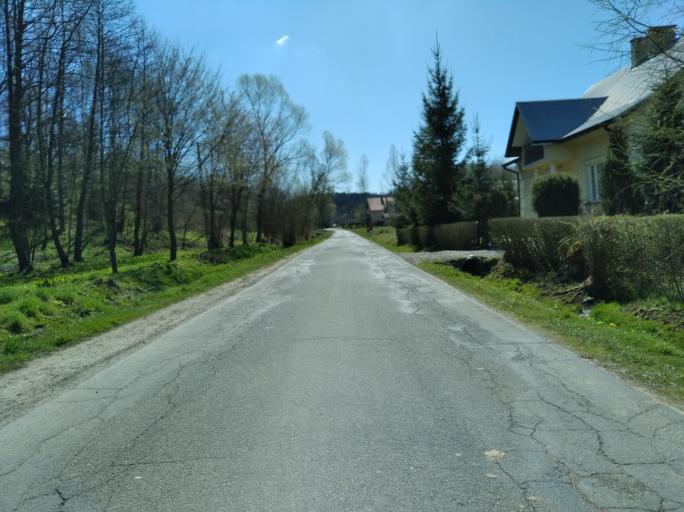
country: PL
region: Subcarpathian Voivodeship
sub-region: Powiat brzozowski
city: Jablonka
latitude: 49.7328
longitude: 22.1465
